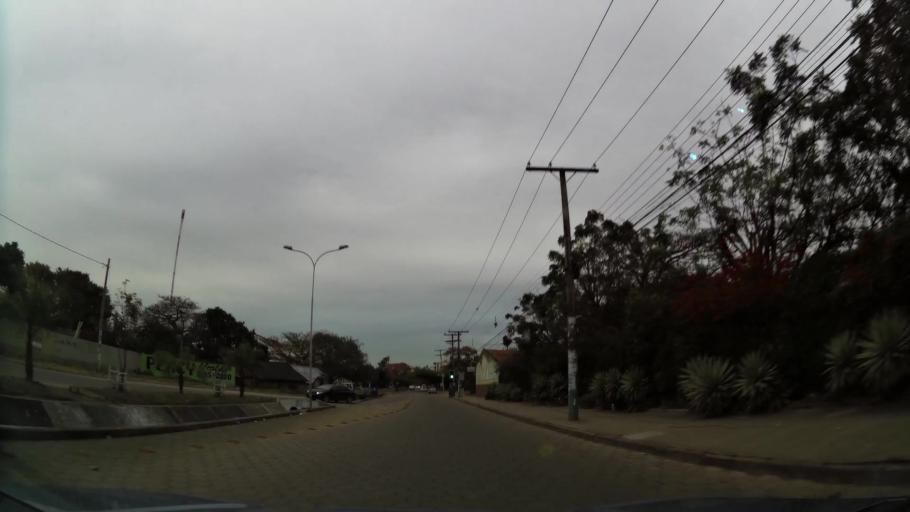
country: BO
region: Santa Cruz
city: Santa Cruz de la Sierra
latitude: -17.7784
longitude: -63.1994
